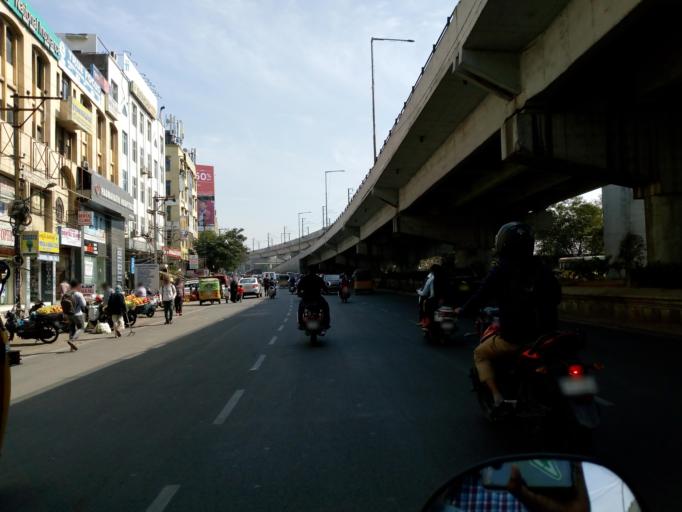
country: IN
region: Telangana
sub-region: Hyderabad
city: Malkajgiri
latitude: 17.4263
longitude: 78.5319
